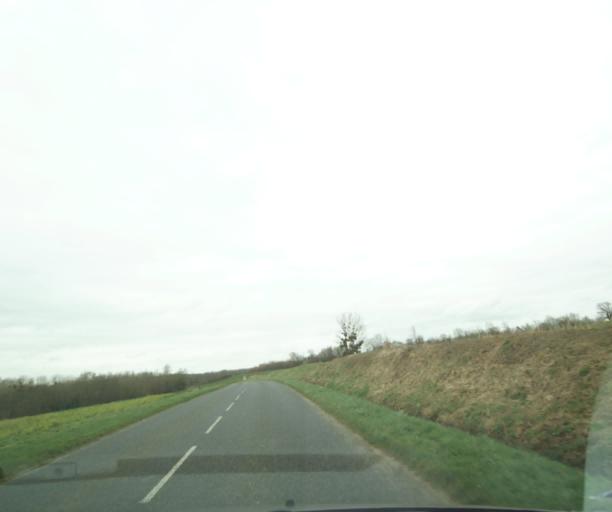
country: FR
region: Picardie
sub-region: Departement de l'Oise
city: Noyon
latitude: 49.5934
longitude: 2.9934
